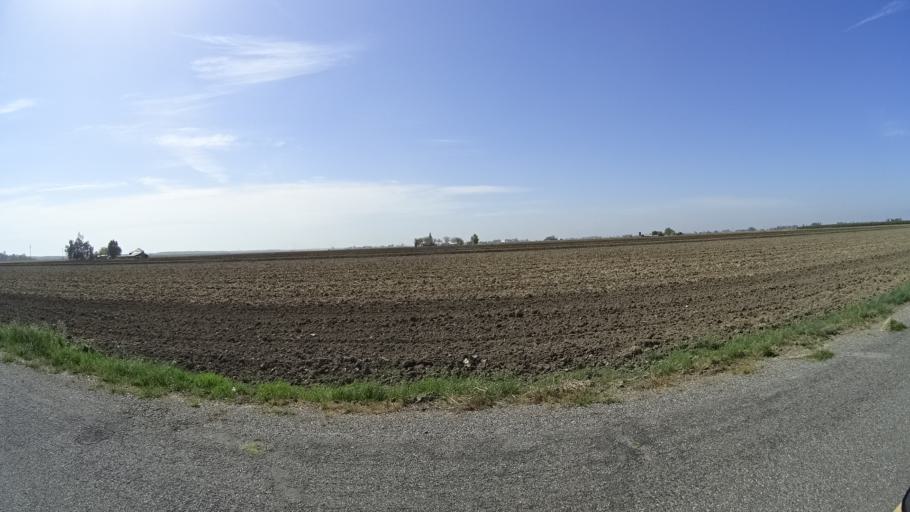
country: US
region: California
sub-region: Glenn County
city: Hamilton City
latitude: 39.6163
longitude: -122.0317
